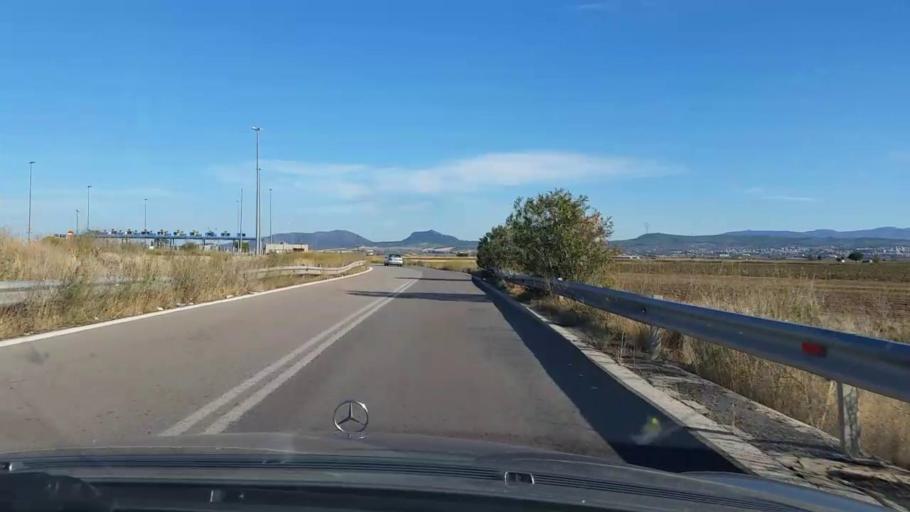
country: GR
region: Central Greece
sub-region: Nomos Voiotias
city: Thivai
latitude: 38.3715
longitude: 23.2833
